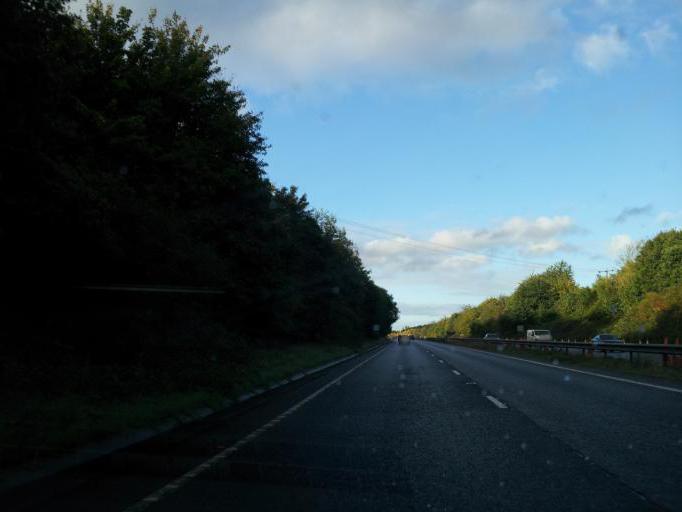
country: GB
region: England
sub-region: Norfolk
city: Thorpe Hamlet
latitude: 52.6191
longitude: 1.3527
